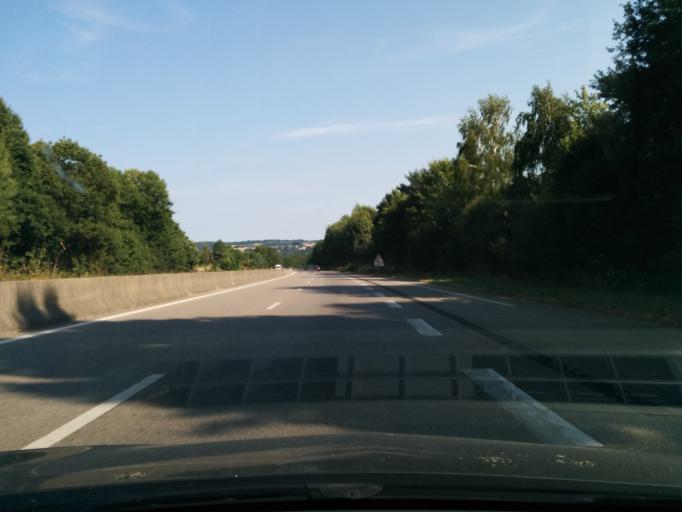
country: FR
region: Limousin
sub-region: Departement de la Haute-Vienne
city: Boisseuil
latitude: 45.7517
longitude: 1.3349
